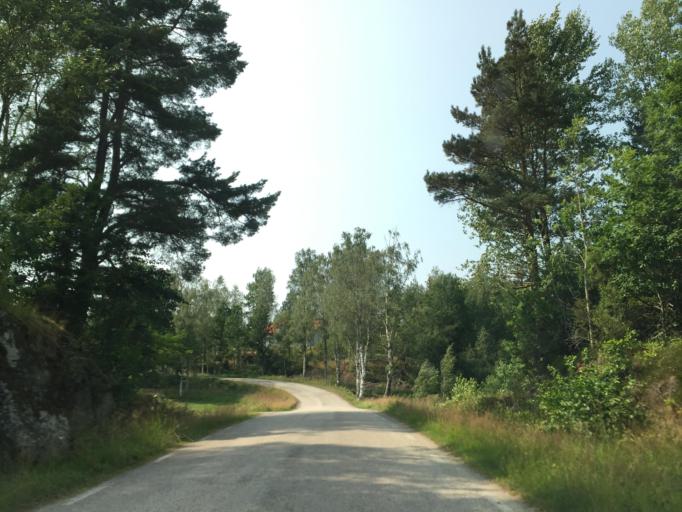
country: SE
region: Vaestra Goetaland
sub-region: Trollhattan
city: Sjuntorp
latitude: 58.3007
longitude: 12.1391
